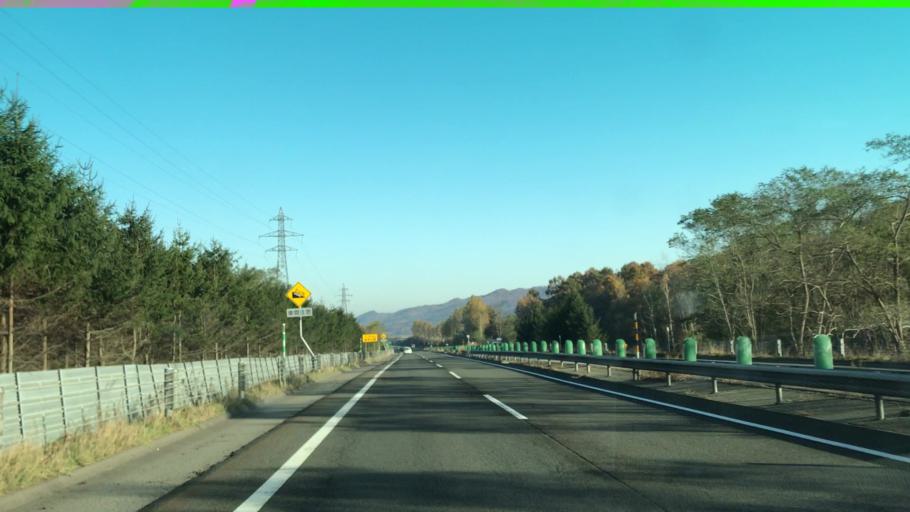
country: JP
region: Hokkaido
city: Sunagawa
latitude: 43.4264
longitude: 141.9126
